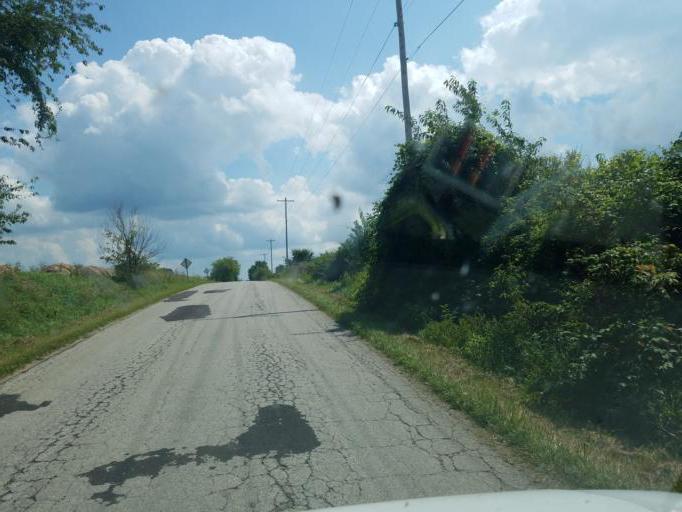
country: US
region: Ohio
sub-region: Knox County
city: Centerburg
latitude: 40.4072
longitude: -82.6742
